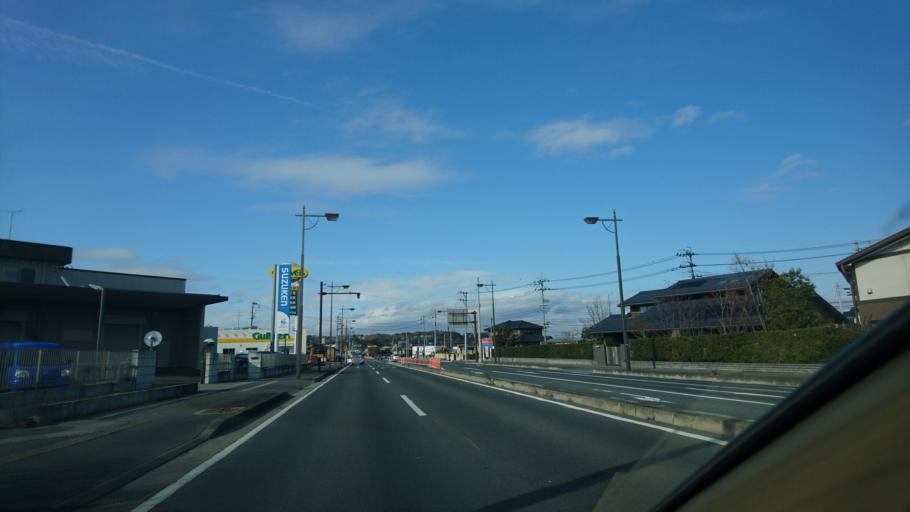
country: JP
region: Miyagi
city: Ishinomaki
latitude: 38.4509
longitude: 141.2665
